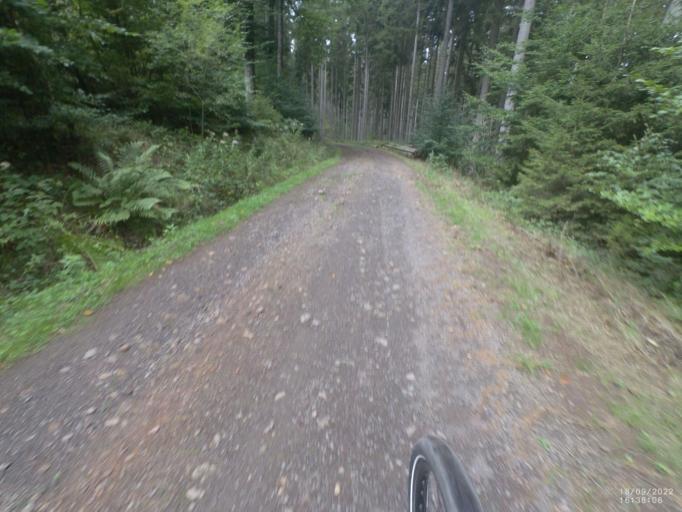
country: DE
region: Rheinland-Pfalz
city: Weidenbach
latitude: 50.1155
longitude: 6.7084
